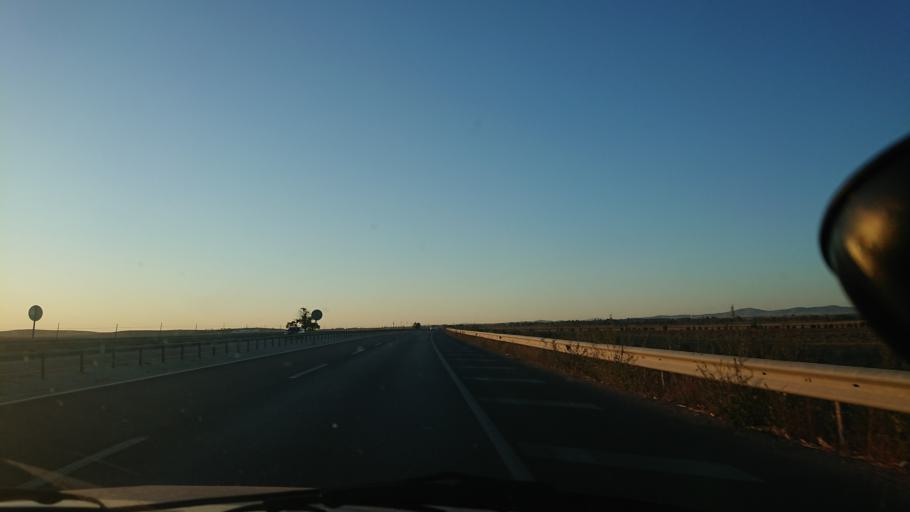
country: TR
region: Eskisehir
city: Mahmudiye
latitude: 39.5445
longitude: 30.9340
